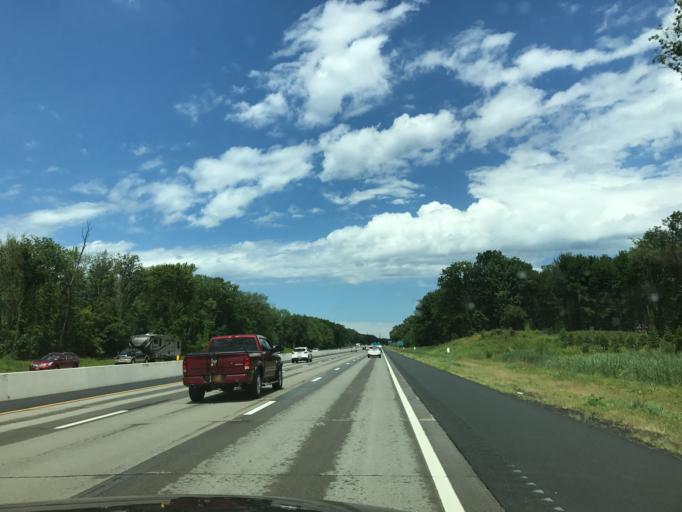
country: US
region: New York
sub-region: Albany County
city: McKownville
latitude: 42.6668
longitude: -73.8339
